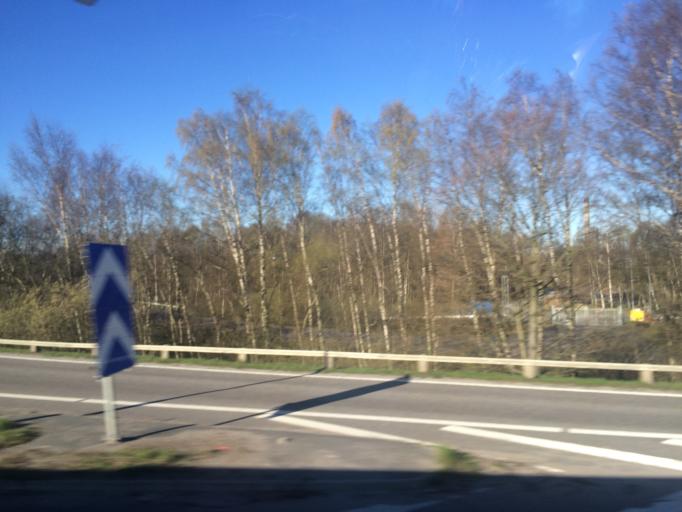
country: SE
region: Vaestra Goetaland
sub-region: Goteborg
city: Majorna
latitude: 57.7008
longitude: 11.8942
